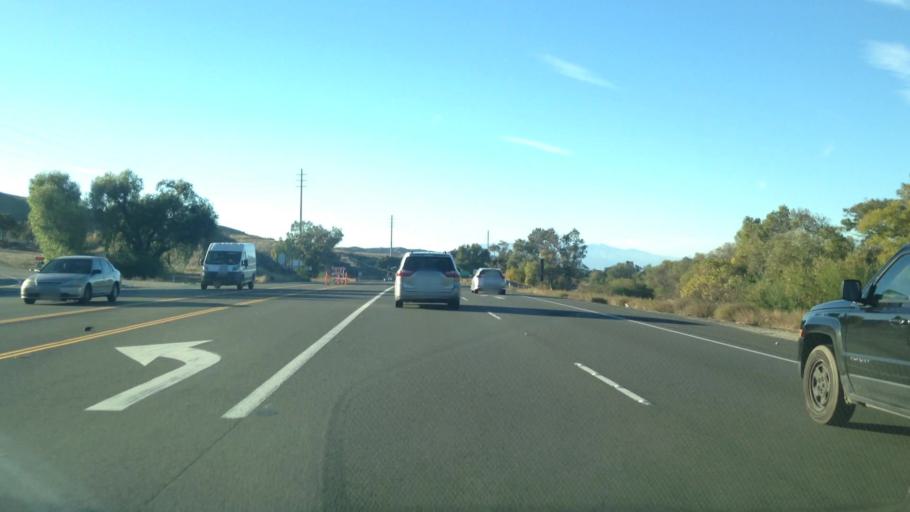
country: US
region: California
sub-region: Riverside County
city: Beaumont
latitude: 33.9336
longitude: -117.0324
